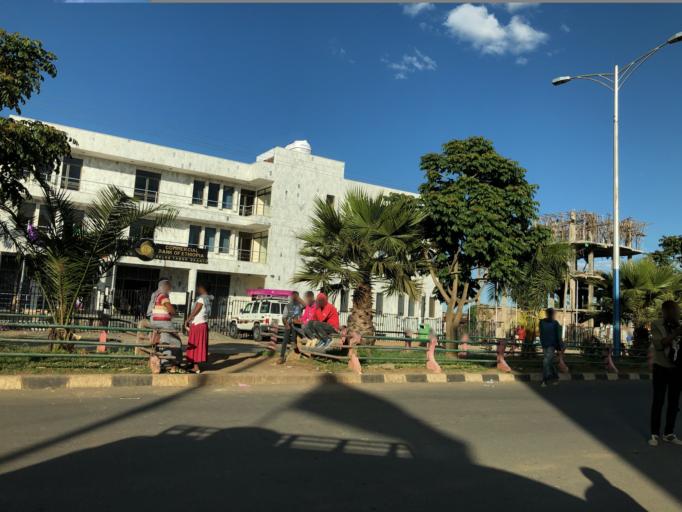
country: ET
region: Amhara
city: Debre Tabor
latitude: 11.8578
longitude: 38.0047
